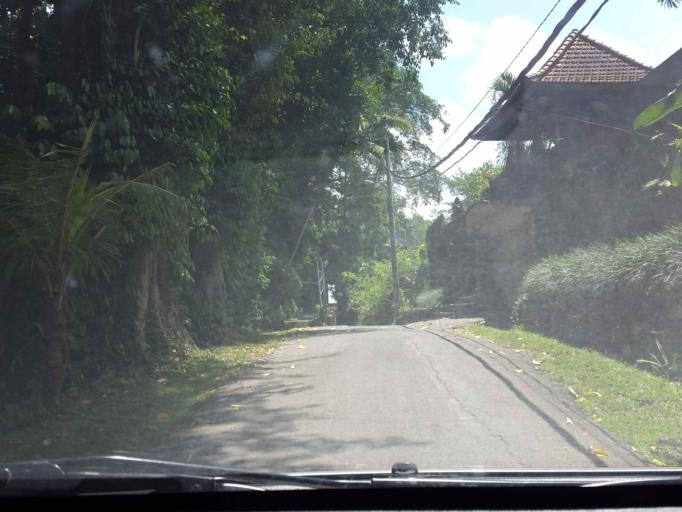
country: ID
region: Bali
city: Banjar Wangsian
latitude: -8.4931
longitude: 115.4002
